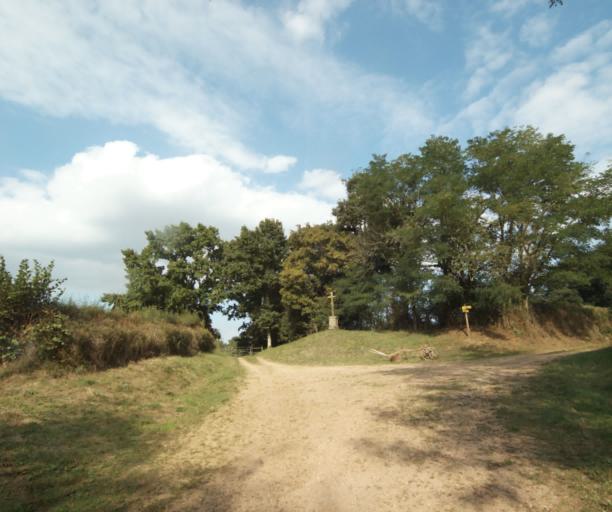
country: FR
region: Bourgogne
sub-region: Departement de Saone-et-Loire
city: Palinges
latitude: 46.5133
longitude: 4.2657
